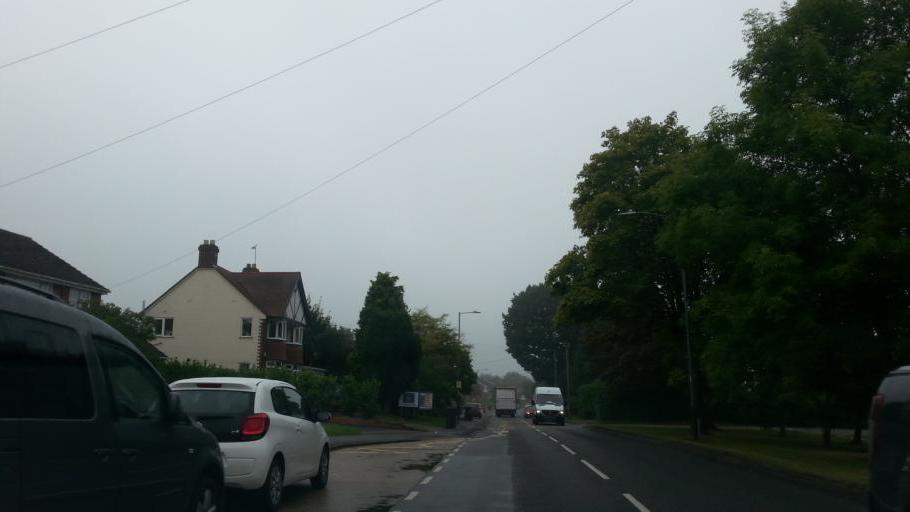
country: GB
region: England
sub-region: Warwickshire
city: Kenilworth
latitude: 52.3555
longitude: -1.5932
